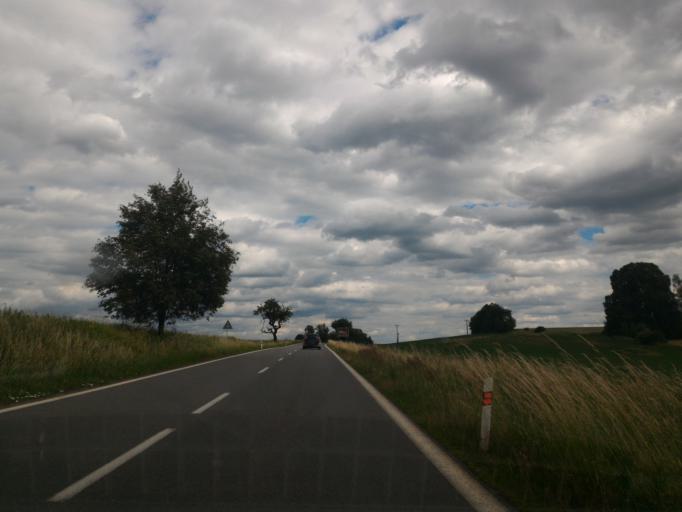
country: CZ
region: Vysocina
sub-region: Okres Jihlava
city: Telc
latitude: 49.1848
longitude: 15.4202
